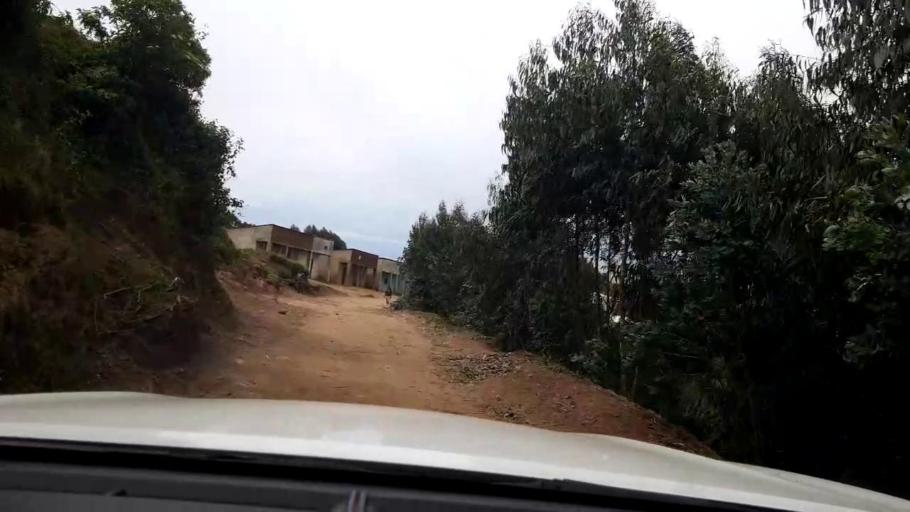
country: RW
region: Western Province
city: Kibuye
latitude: -1.8819
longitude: 29.4543
